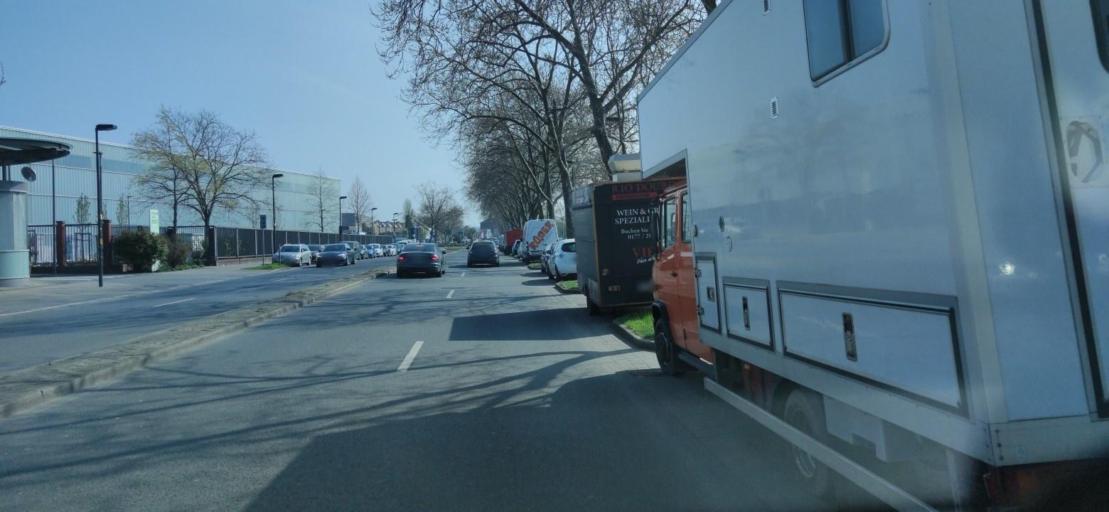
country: DE
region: North Rhine-Westphalia
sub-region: Regierungsbezirk Dusseldorf
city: Dusseldorf
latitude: 51.2218
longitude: 6.8176
